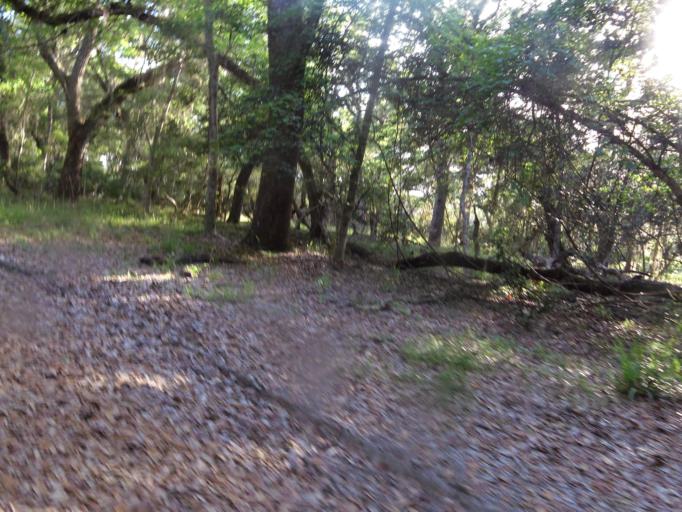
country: US
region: Florida
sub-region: Saint Johns County
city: Villano Beach
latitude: 30.0248
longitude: -81.3357
